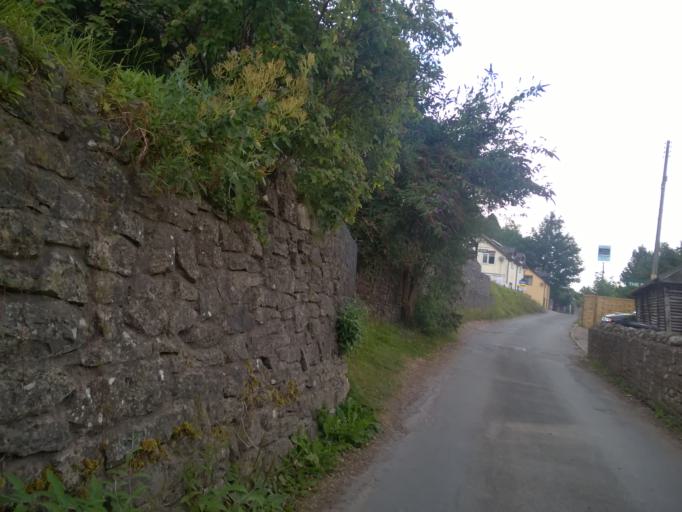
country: GB
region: England
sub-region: Herefordshire
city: Whitchurch
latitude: 51.8461
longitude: -2.6461
